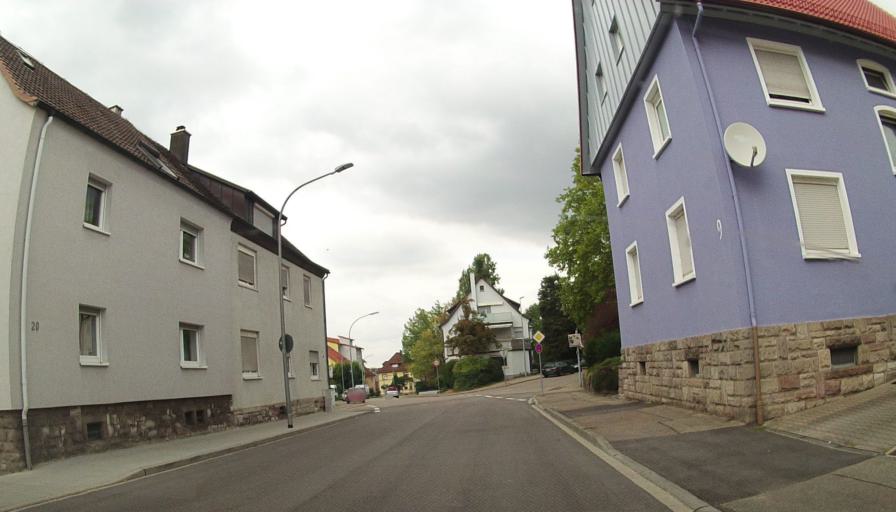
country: DE
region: Baden-Wuerttemberg
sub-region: Karlsruhe Region
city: Gaggenau
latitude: 48.8026
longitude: 8.3249
